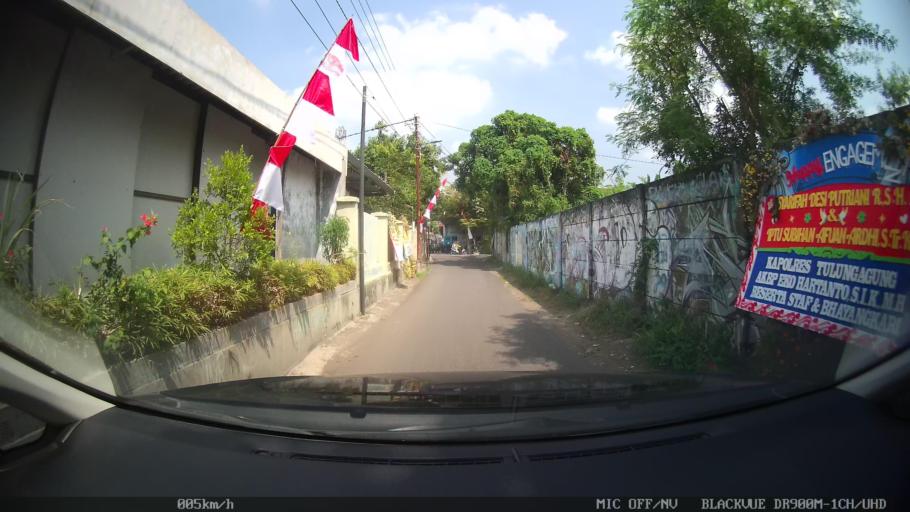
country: ID
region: Daerah Istimewa Yogyakarta
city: Yogyakarta
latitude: -7.8134
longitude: 110.3836
